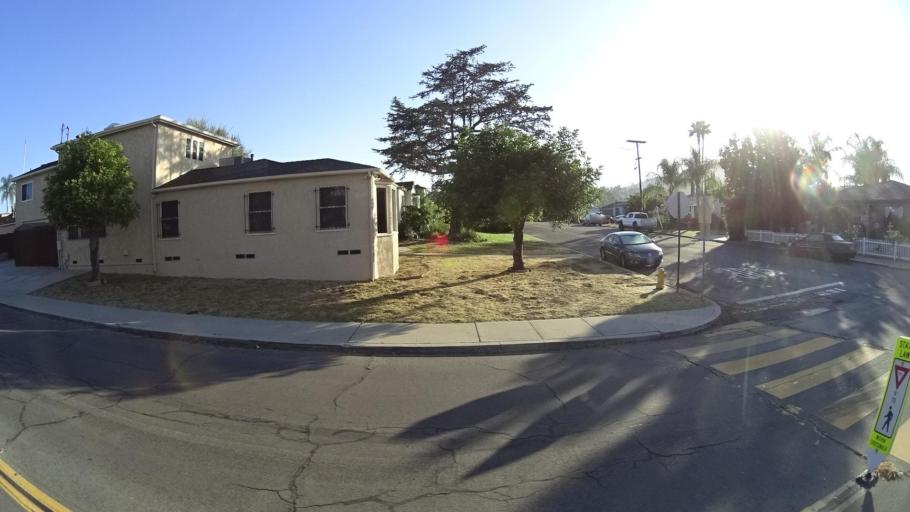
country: US
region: California
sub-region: San Diego County
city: La Mesa
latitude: 32.7692
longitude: -117.0071
